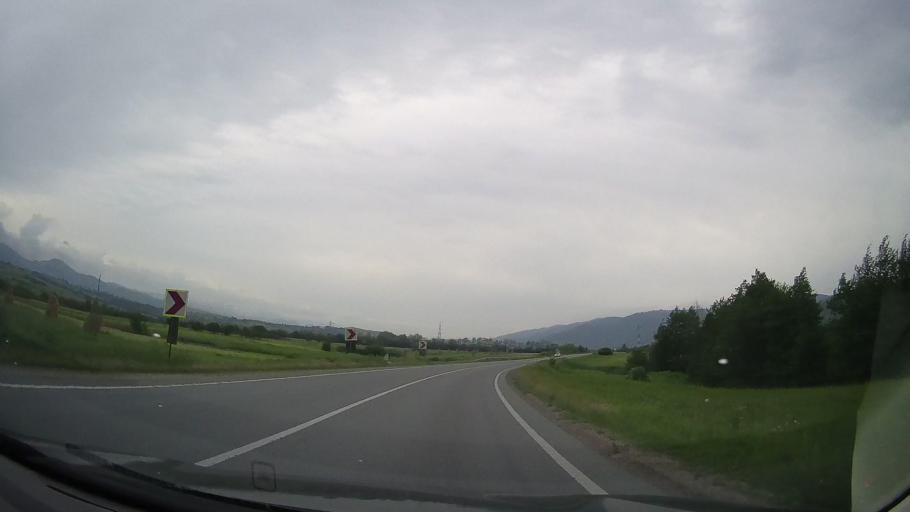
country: RO
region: Caras-Severin
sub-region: Comuna Bucosnita
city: Bucosnita
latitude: 45.2853
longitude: 22.2941
